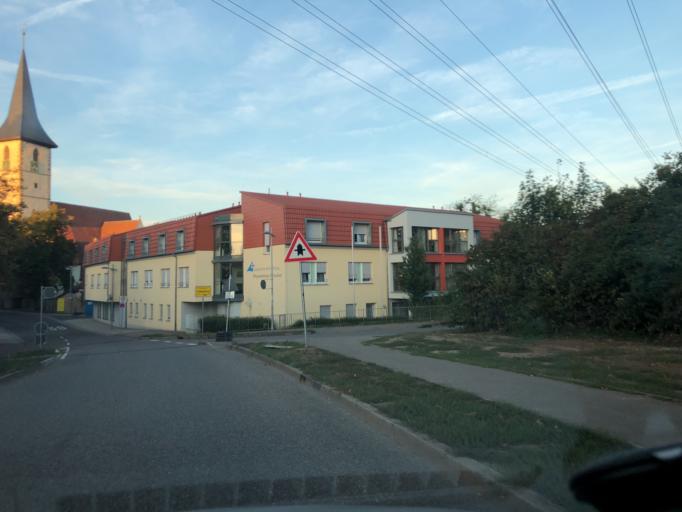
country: DE
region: Baden-Wuerttemberg
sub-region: Regierungsbezirk Stuttgart
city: Freiberg am Neckar
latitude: 48.9085
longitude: 9.2216
